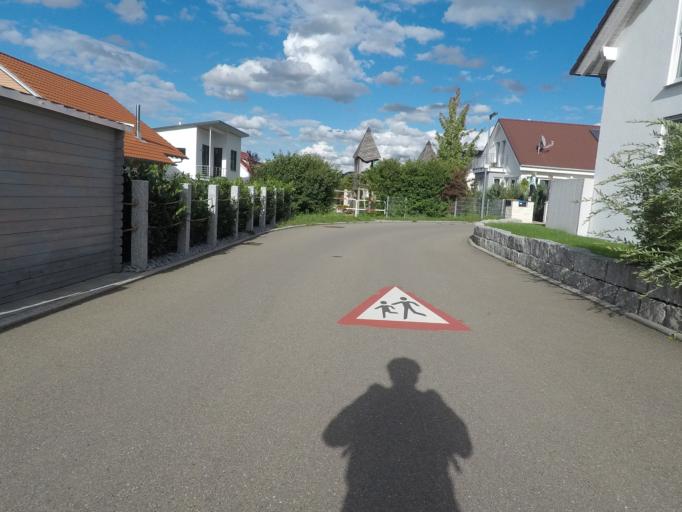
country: DE
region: Baden-Wuerttemberg
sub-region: Tuebingen Region
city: Pfullingen
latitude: 48.4542
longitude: 9.2171
